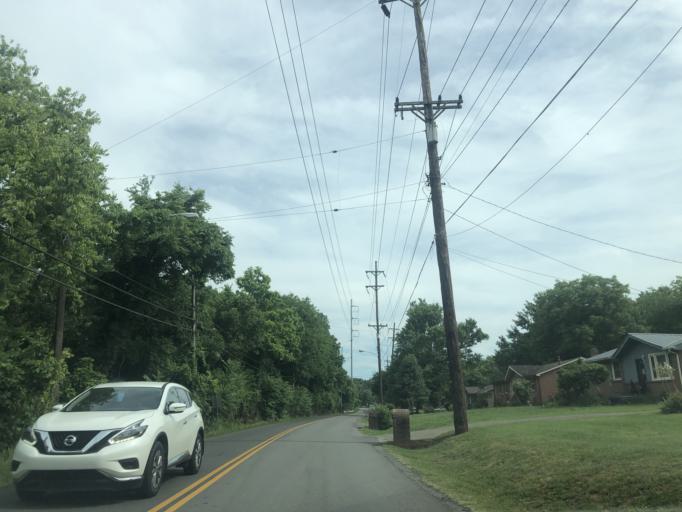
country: US
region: Tennessee
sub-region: Davidson County
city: Nashville
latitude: 36.2225
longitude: -86.8217
